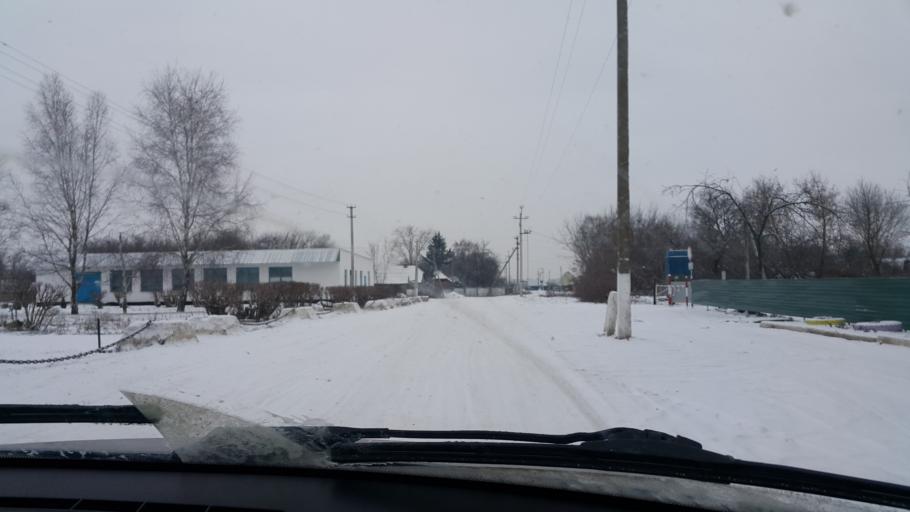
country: RU
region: Tambov
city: Inzhavino
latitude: 52.4683
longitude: 42.3820
